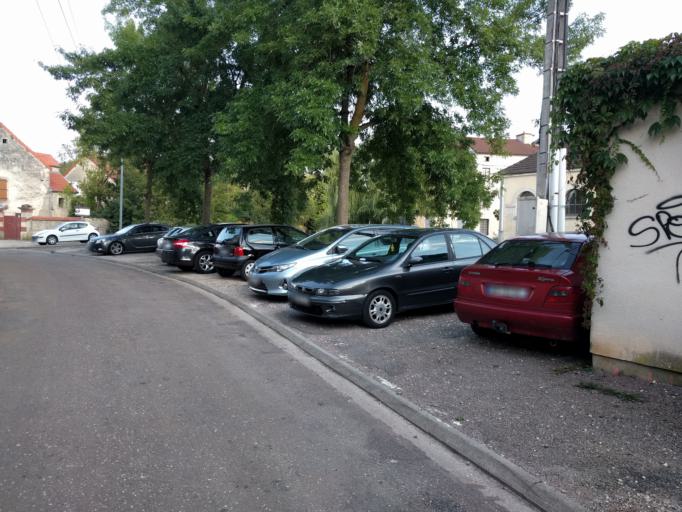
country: FR
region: Bourgogne
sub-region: Departement de la Cote-d'Or
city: Is-sur-Tille
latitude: 47.5244
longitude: 5.1122
